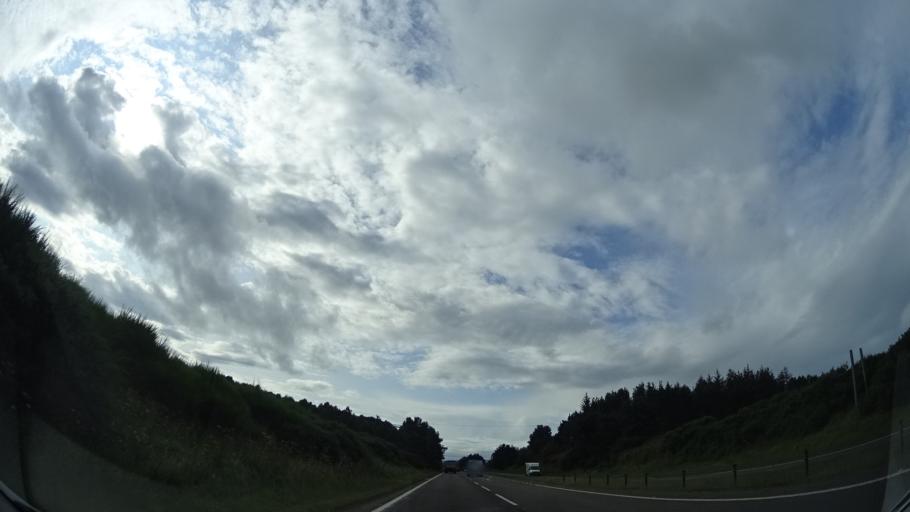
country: GB
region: Scotland
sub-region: Highland
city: Conon Bridge
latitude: 57.5329
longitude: -4.3280
